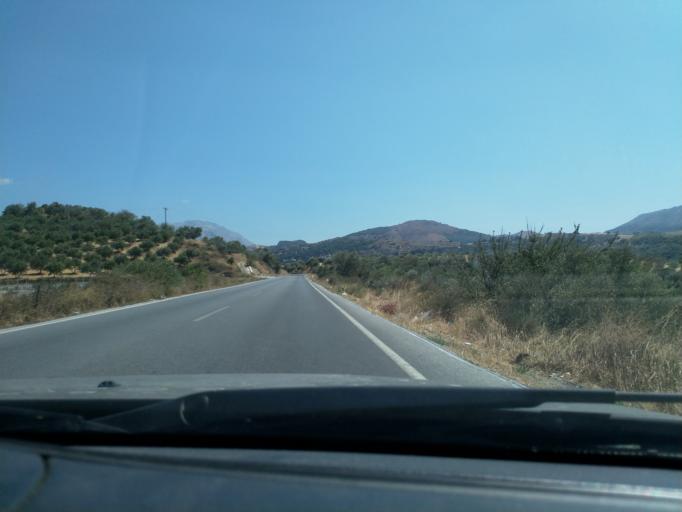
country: GR
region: Crete
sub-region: Nomos Rethymnis
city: Atsipopoulon
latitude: 35.2259
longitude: 24.4792
